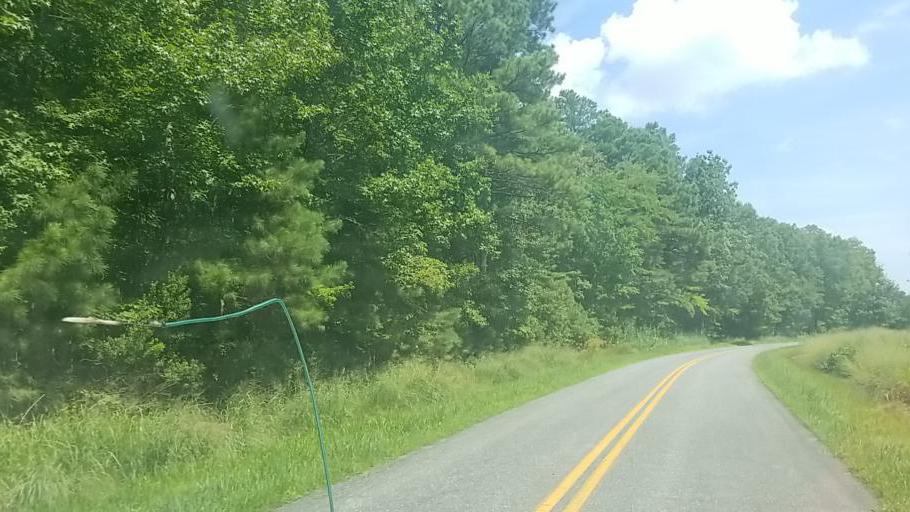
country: US
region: Maryland
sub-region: Dorchester County
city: Hurlock
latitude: 38.4323
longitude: -75.8877
